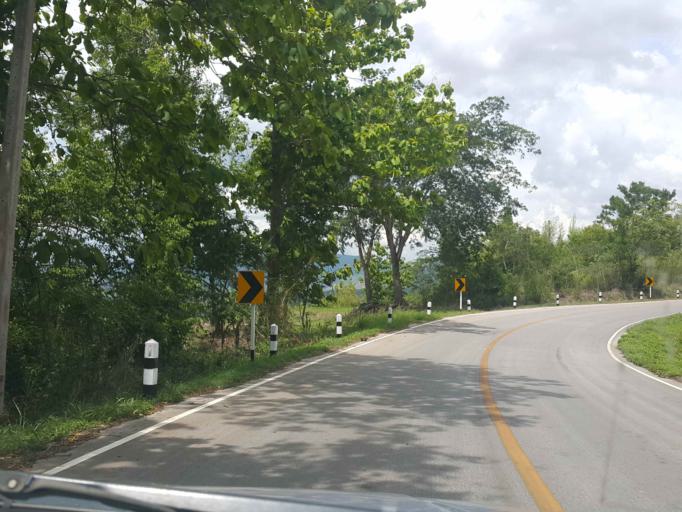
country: TH
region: Nan
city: Ban Luang
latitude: 18.8454
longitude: 100.4026
